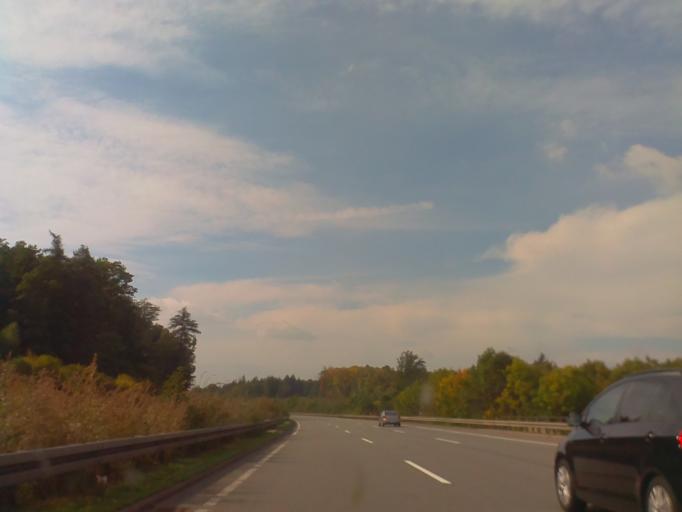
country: DE
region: Thuringia
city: Emleben
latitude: 50.9076
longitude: 10.6624
